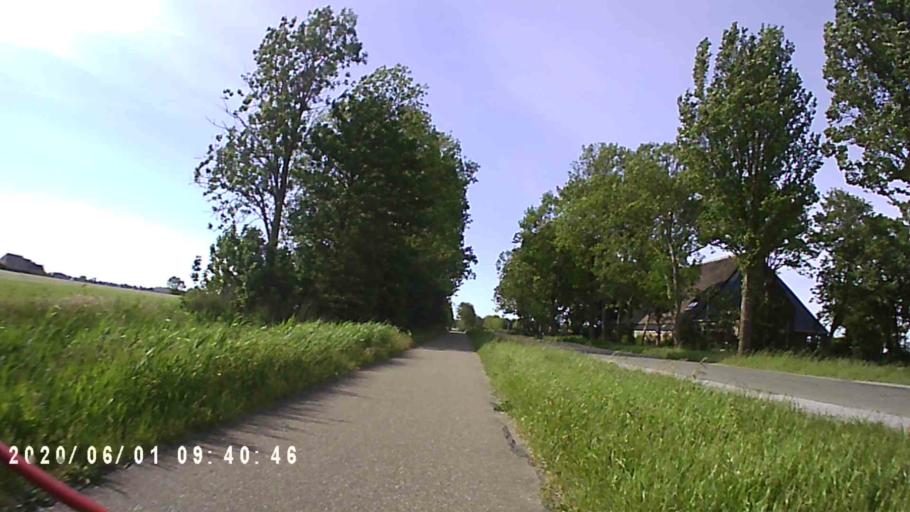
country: NL
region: Friesland
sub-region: Menameradiel
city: Berltsum
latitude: 53.2508
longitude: 5.6816
